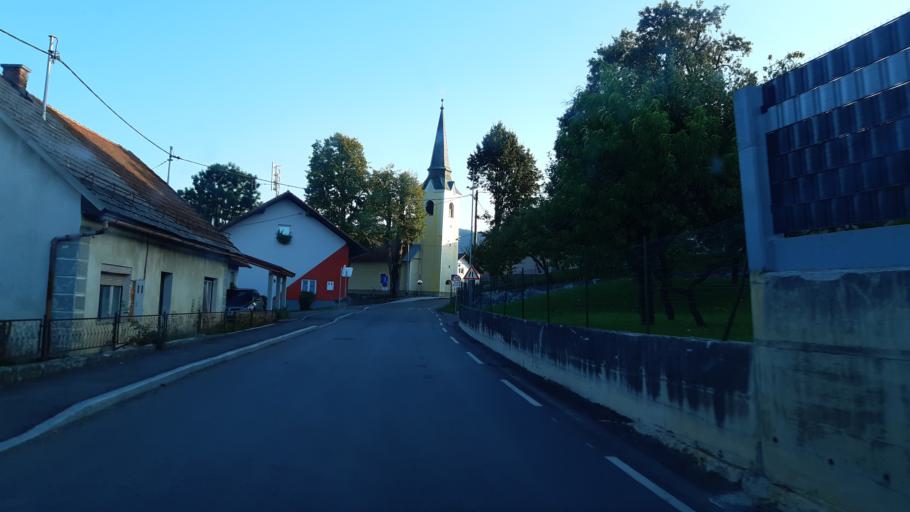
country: SI
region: Kocevje
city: Kocevje
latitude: 45.6465
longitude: 14.8800
